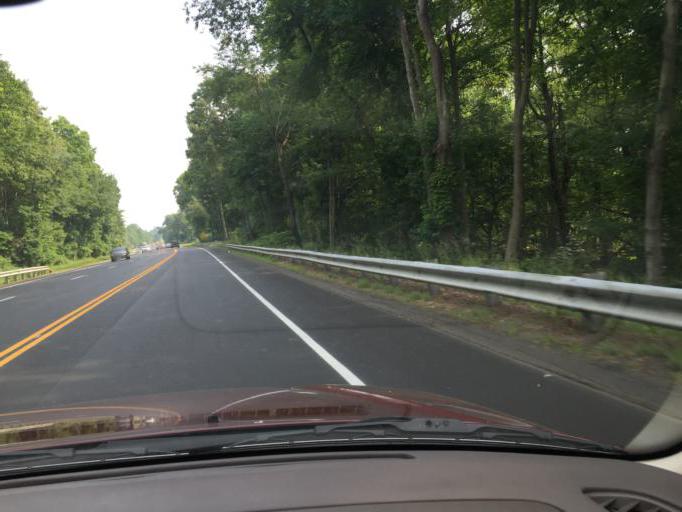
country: US
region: Connecticut
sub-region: Fairfield County
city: Westport
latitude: 41.1324
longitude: -73.3344
